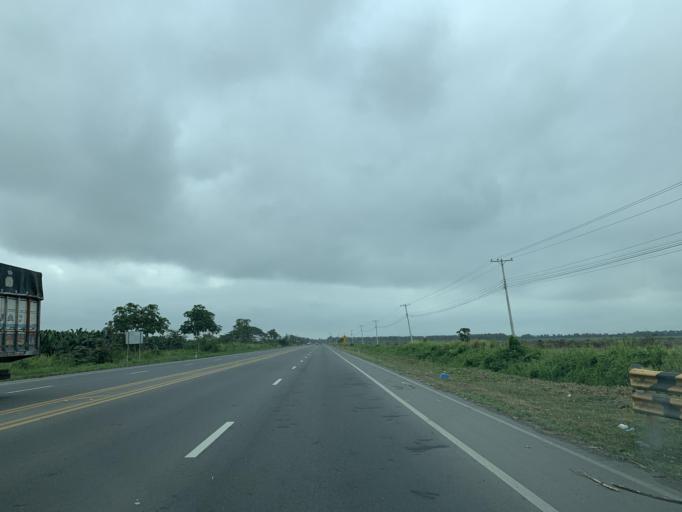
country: EC
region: Guayas
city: Coronel Marcelino Mariduena
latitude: -2.2958
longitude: -79.4976
